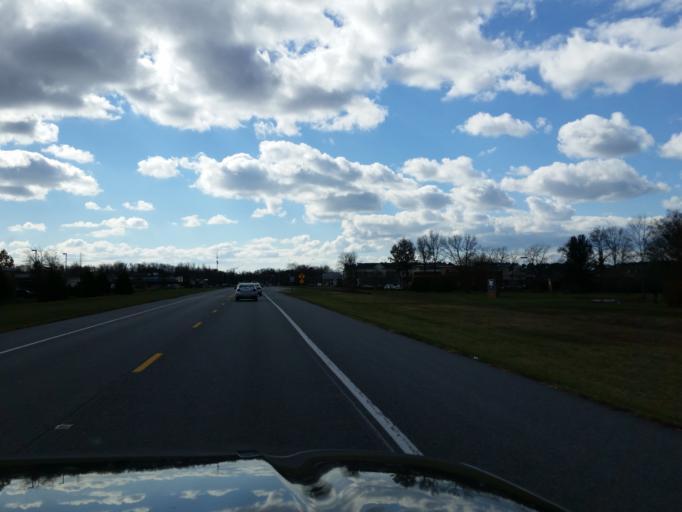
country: US
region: Maryland
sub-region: Talbot County
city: Easton
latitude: 38.7846
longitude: -76.0810
